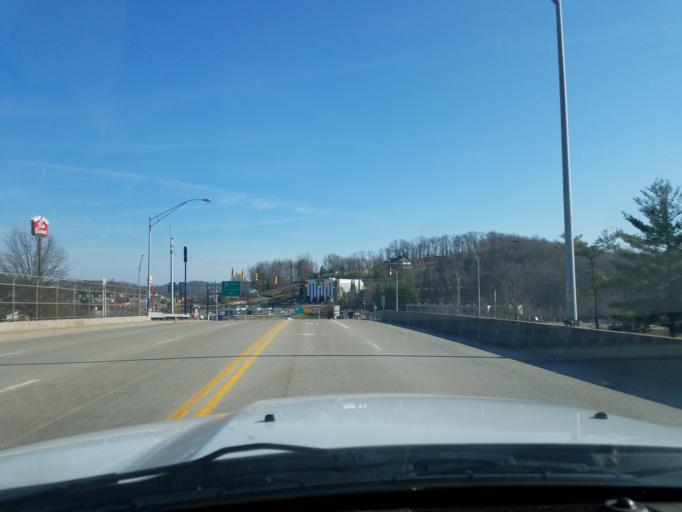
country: US
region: West Virginia
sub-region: Kanawha County
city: Cross Lanes
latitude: 38.4133
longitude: -81.7966
